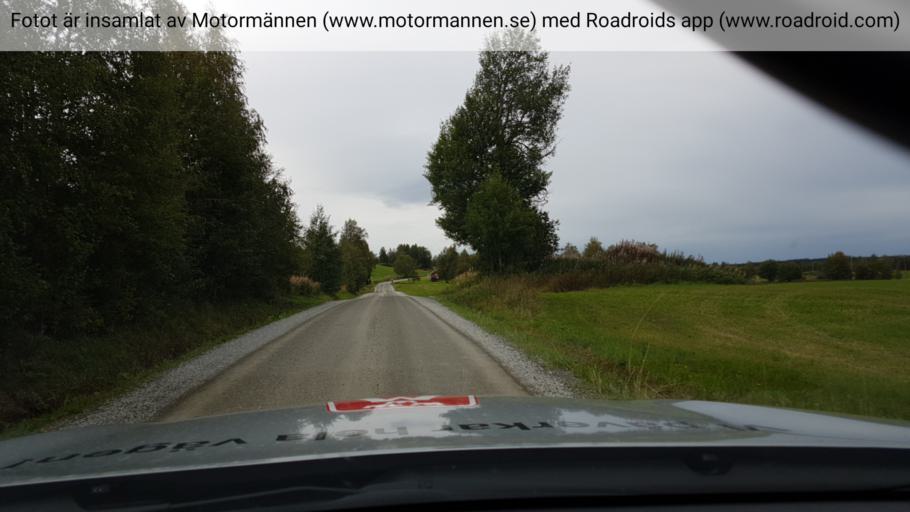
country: SE
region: Jaemtland
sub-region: Bergs Kommun
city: Hoverberg
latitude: 62.9368
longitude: 14.2776
